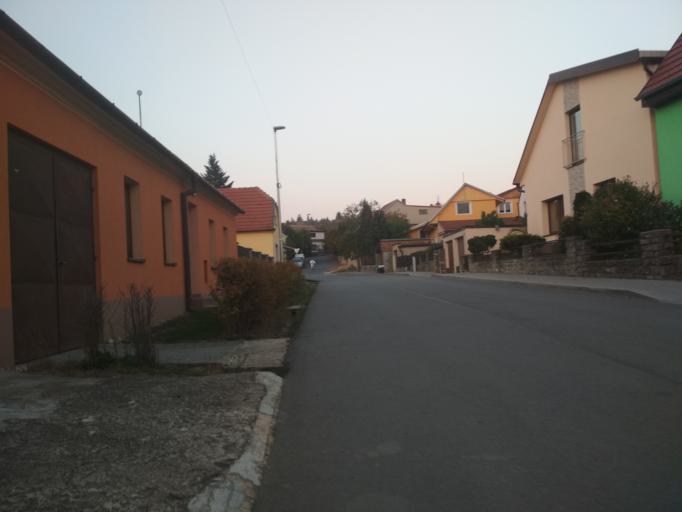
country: CZ
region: South Moravian
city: Bilovice nad Svitavou
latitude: 49.2859
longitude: 16.6977
